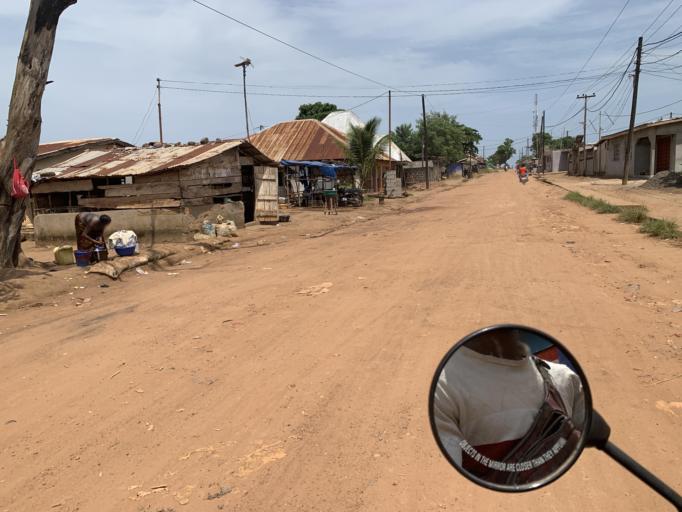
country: SL
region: Western Area
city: Hastings
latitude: 8.4056
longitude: -13.1347
